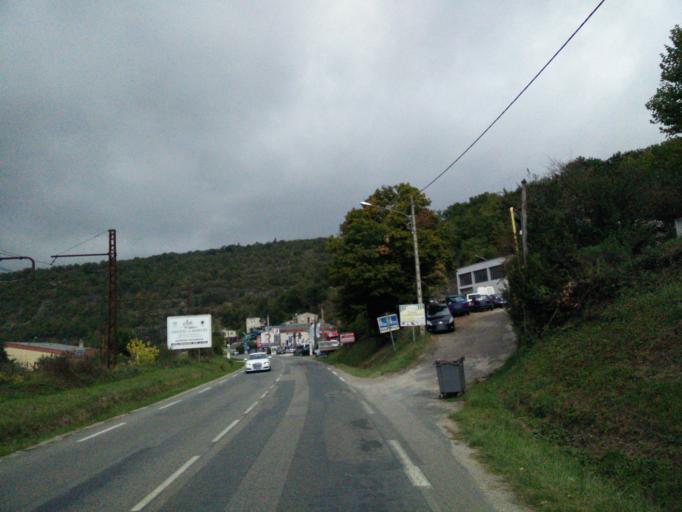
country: FR
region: Midi-Pyrenees
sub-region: Departement du Lot
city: Cahors
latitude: 44.4729
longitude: 1.4286
